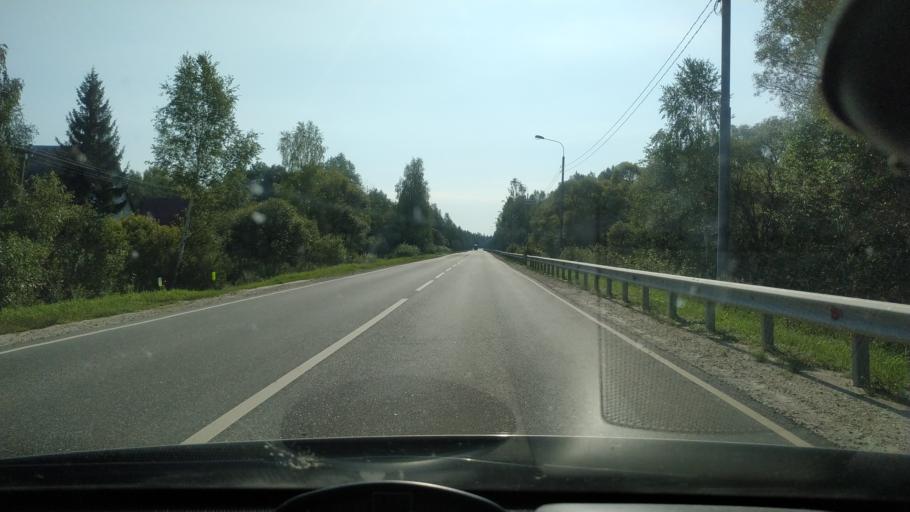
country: RU
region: Moskovskaya
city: Dmitrovskiy Pogost
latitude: 55.2318
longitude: 39.9136
